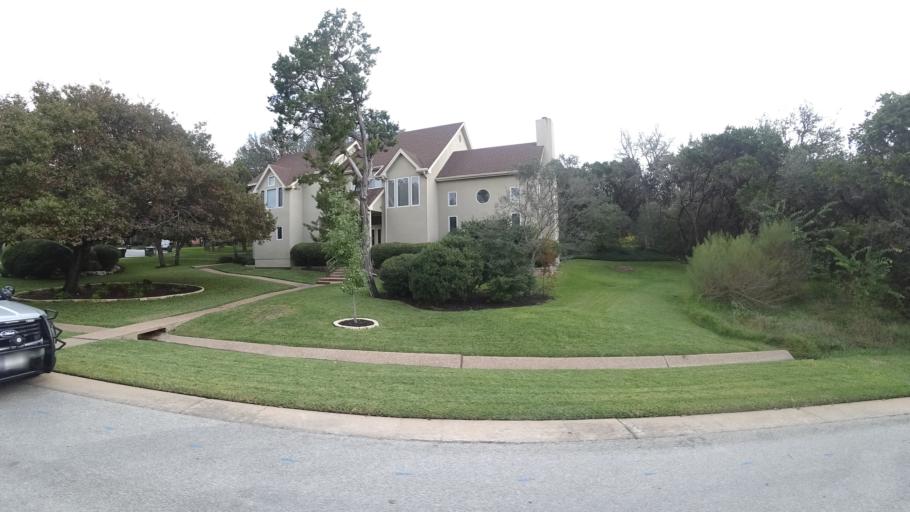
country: US
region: Texas
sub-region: Travis County
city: Barton Creek
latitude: 30.2986
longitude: -97.8937
